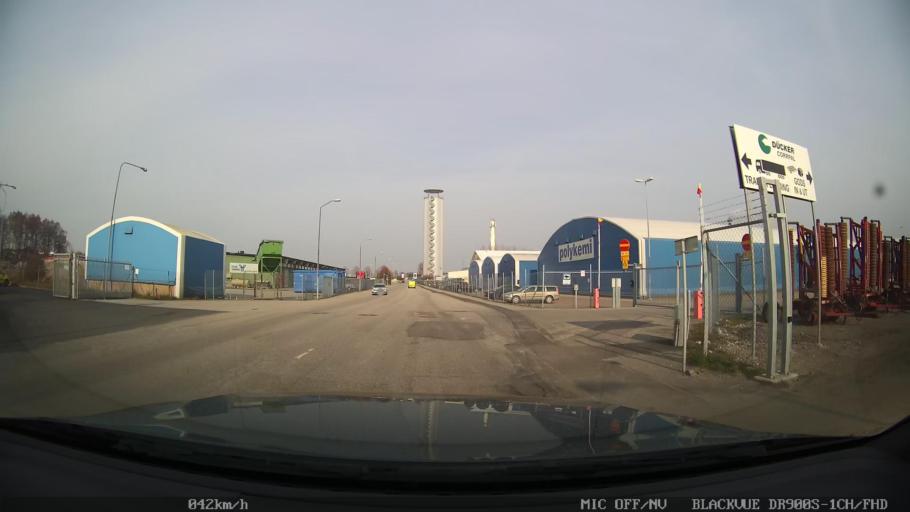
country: SE
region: Skane
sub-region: Ystads Kommun
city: Ystad
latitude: 55.4401
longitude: 13.8387
